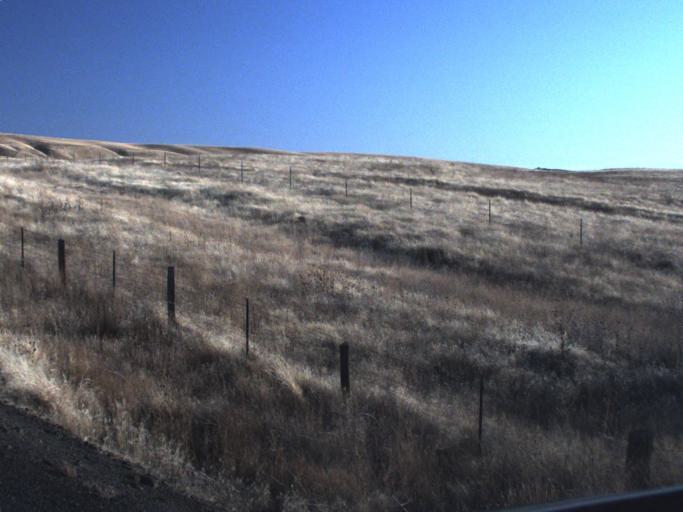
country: US
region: Washington
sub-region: Walla Walla County
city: Waitsburg
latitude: 46.6604
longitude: -118.2705
